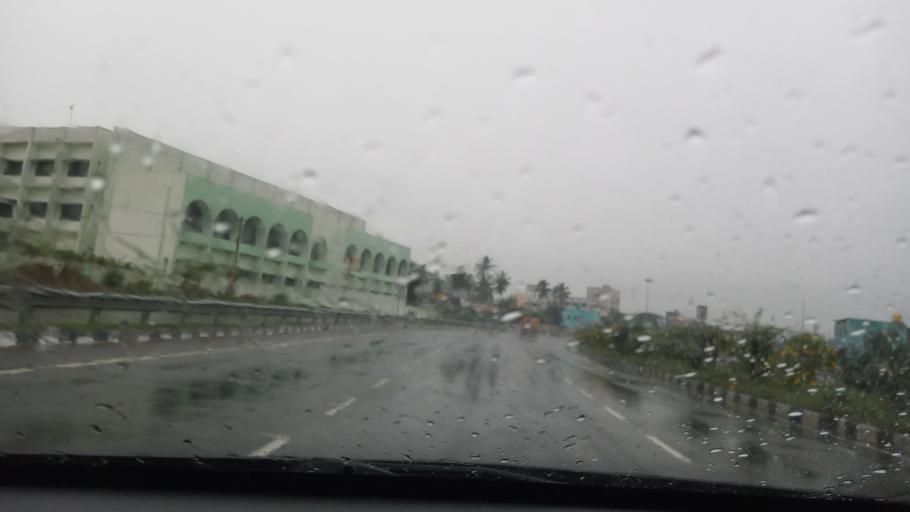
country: IN
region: Tamil Nadu
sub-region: Vellore
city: Arcot
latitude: 12.9257
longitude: 79.2676
